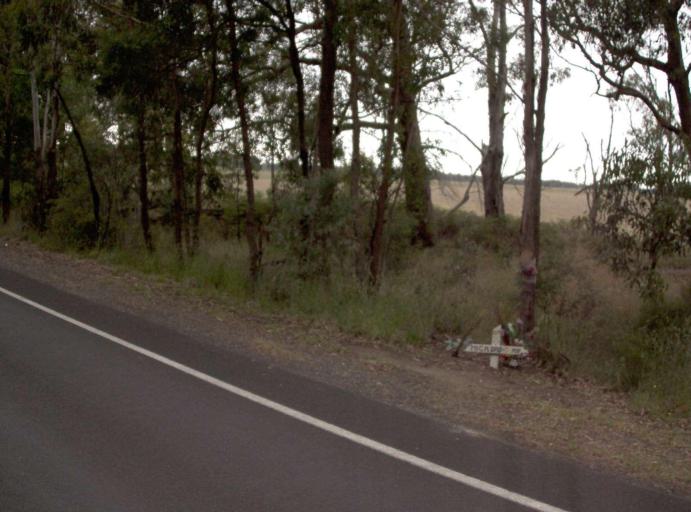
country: AU
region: Victoria
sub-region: Wellington
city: Sale
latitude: -38.4059
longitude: 146.9664
